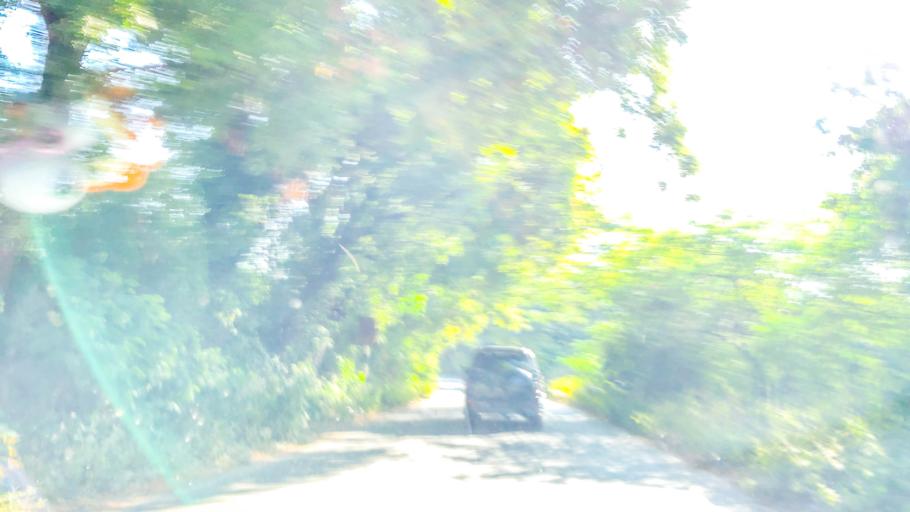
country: MM
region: Sagain
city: Sagaing
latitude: 21.8672
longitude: 95.9976
